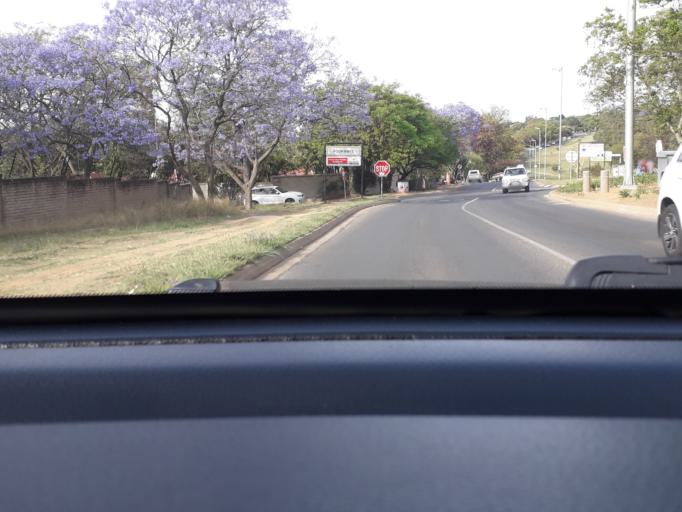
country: ZA
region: Gauteng
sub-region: City of Johannesburg Metropolitan Municipality
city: Diepsloot
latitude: -26.0363
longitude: 27.9998
